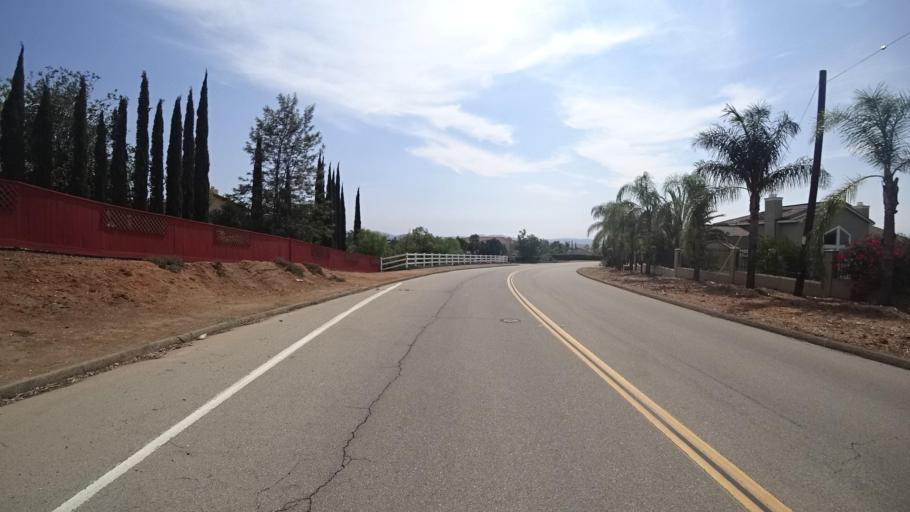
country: US
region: California
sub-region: San Diego County
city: Escondido
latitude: 33.0924
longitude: -117.0435
